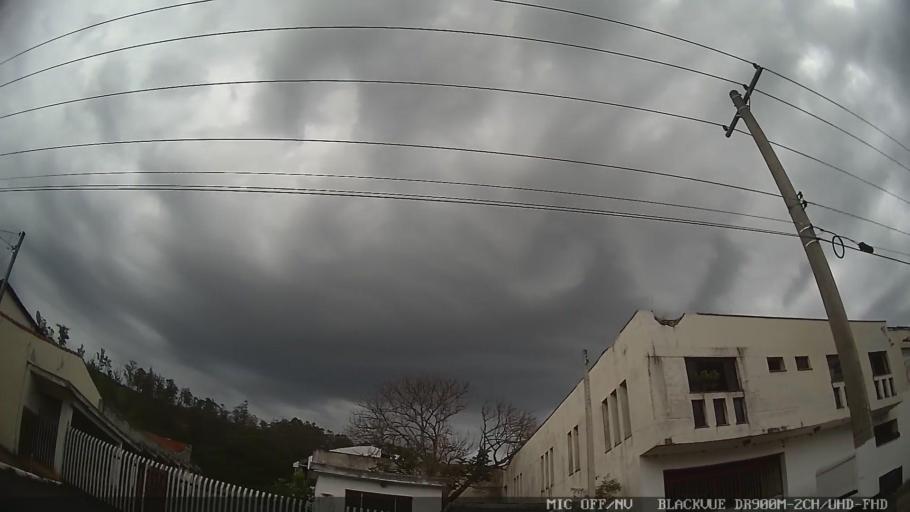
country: BR
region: Sao Paulo
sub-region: Amparo
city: Amparo
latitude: -22.7093
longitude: -46.7842
